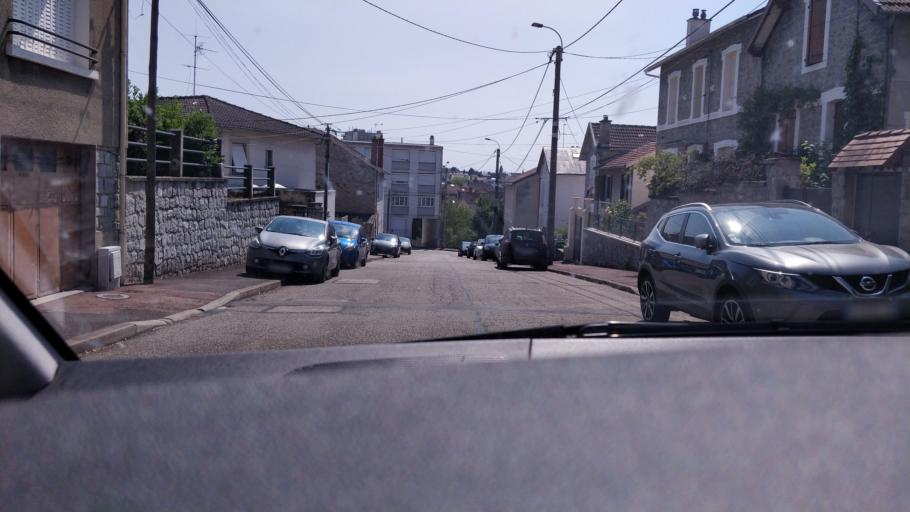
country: FR
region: Limousin
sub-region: Departement de la Haute-Vienne
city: Limoges
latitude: 45.8381
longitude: 1.2439
